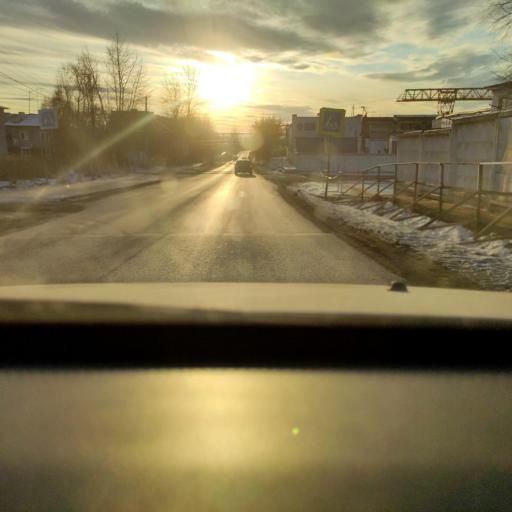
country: RU
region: Perm
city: Ferma
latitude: 57.9114
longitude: 56.3093
